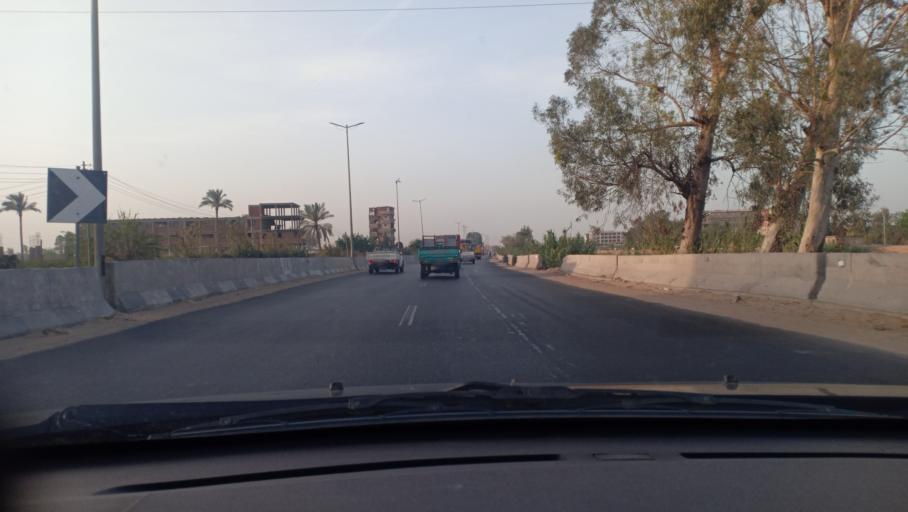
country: EG
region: Muhafazat al Minufiyah
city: Quwaysina
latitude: 30.5589
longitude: 31.2685
